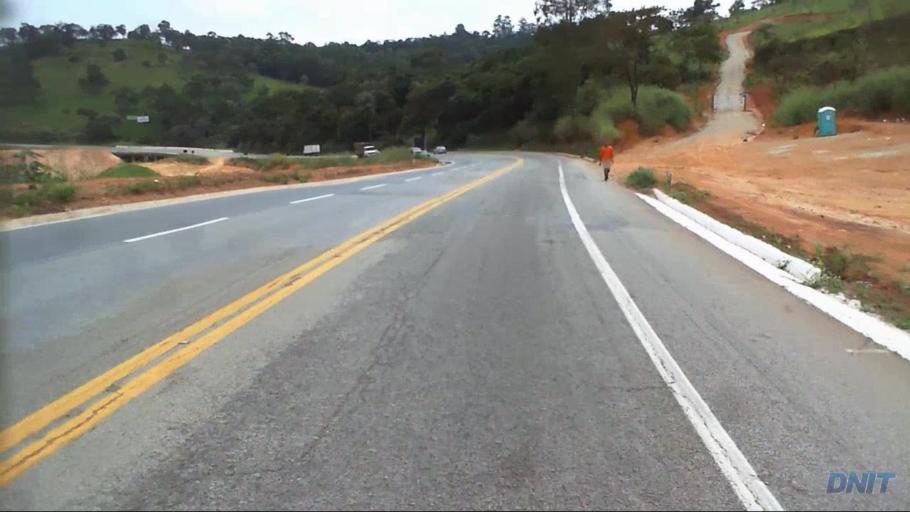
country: BR
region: Minas Gerais
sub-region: Caete
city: Caete
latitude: -19.7472
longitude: -43.6202
